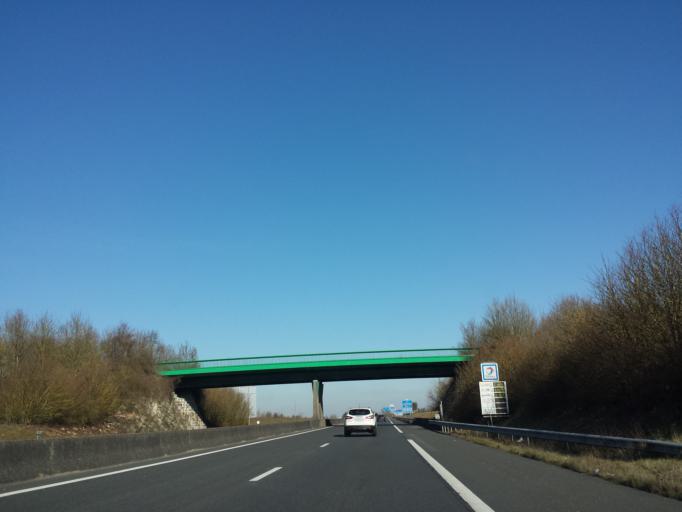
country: FR
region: Picardie
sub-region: Departement de l'Oise
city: Breteuil
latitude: 49.5949
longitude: 2.2027
